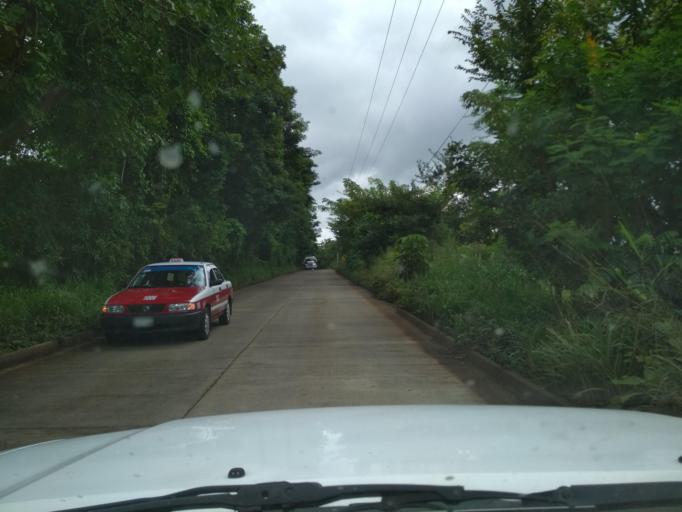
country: MX
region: Veracruz
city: Comoapan
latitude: 18.4170
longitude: -95.1775
